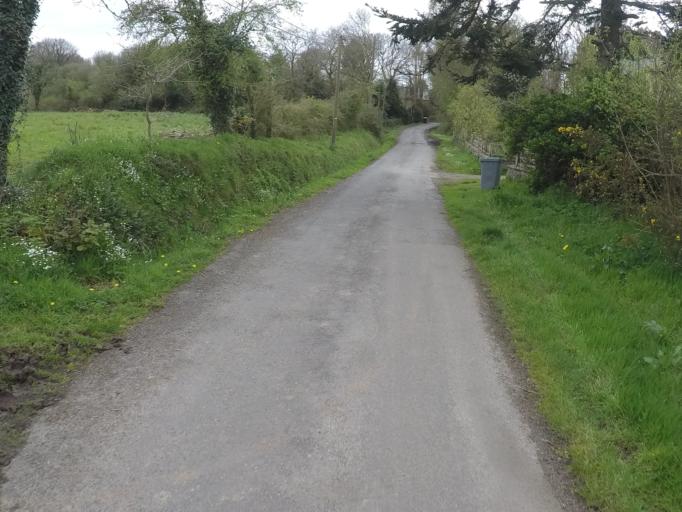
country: FR
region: Brittany
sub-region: Departement des Cotes-d'Armor
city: Plouha
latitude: 48.7003
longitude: -2.9359
